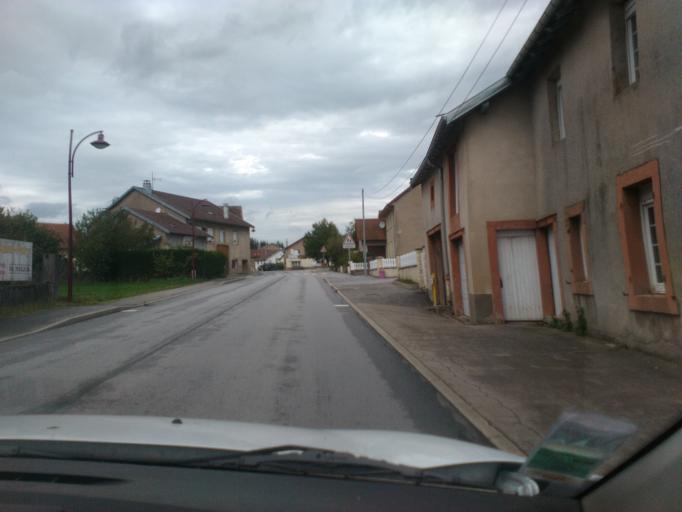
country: FR
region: Lorraine
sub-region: Departement des Vosges
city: Etival-Clairefontaine
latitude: 48.3223
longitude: 6.8285
